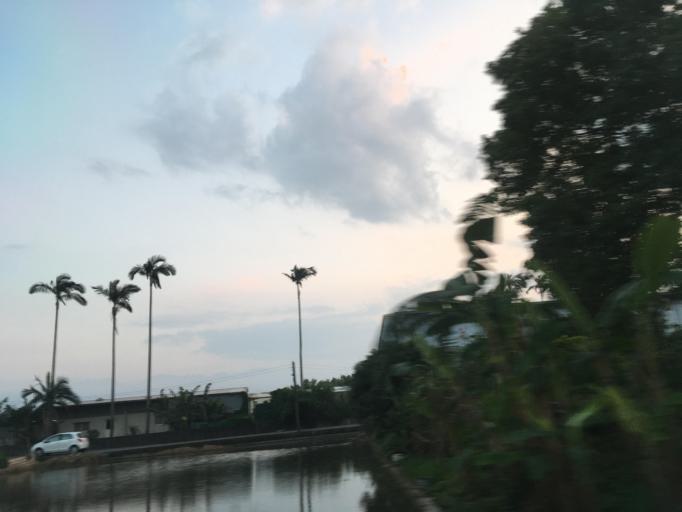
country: TW
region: Taiwan
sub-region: Yilan
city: Yilan
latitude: 24.6908
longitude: 121.7852
